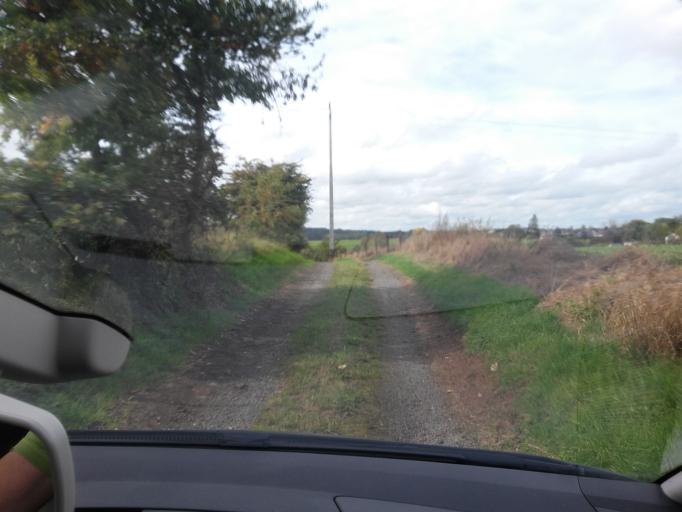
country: BE
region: Wallonia
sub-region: Province du Luxembourg
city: Arlon
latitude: 49.6924
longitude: 5.7942
